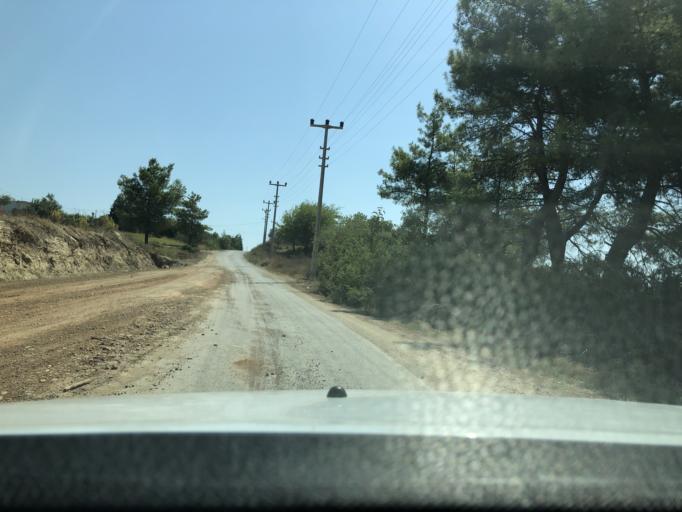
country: TR
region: Antalya
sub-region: Manavgat
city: Manavgat
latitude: 36.8220
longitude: 31.4985
